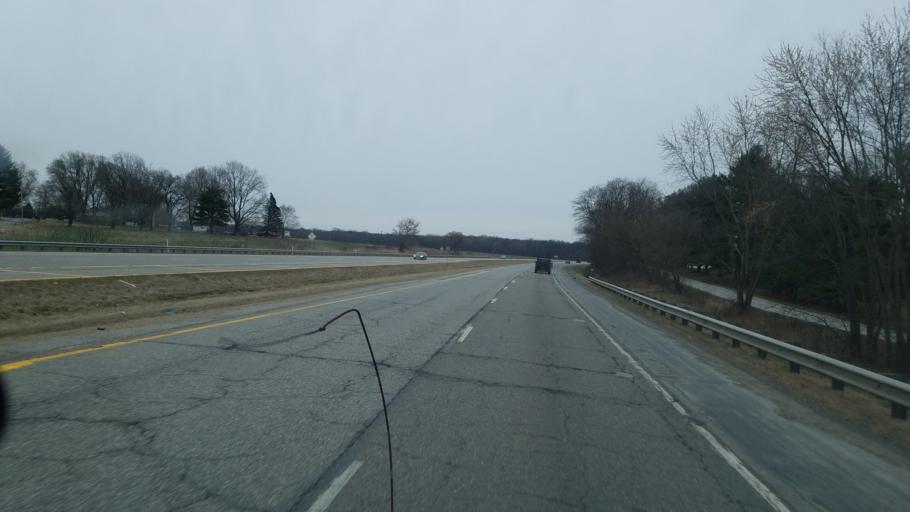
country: US
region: Indiana
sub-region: Marshall County
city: Plymouth
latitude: 41.3602
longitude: -86.2915
